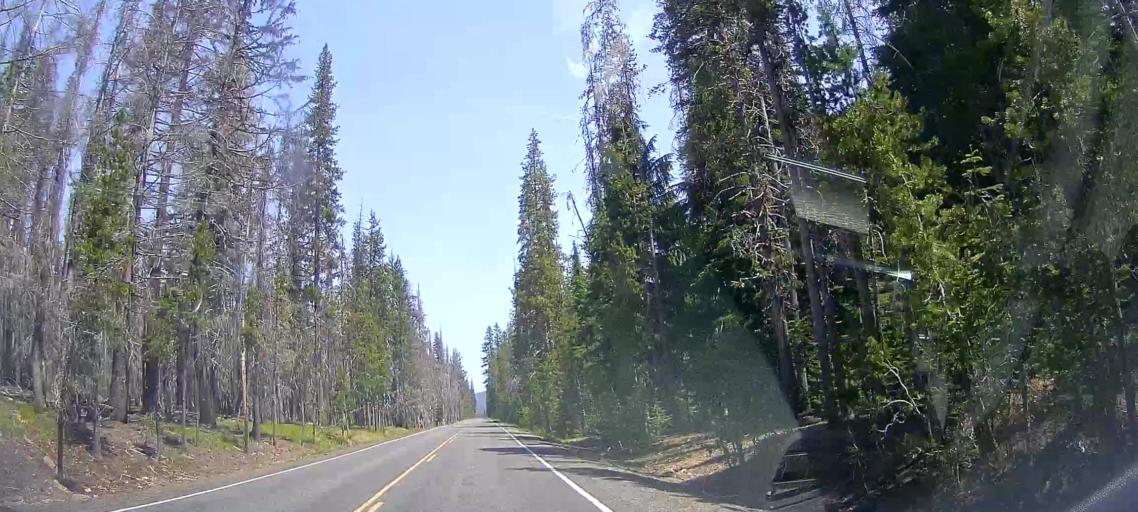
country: US
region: Oregon
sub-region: Lane County
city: Oakridge
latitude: 43.0611
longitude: -122.1211
